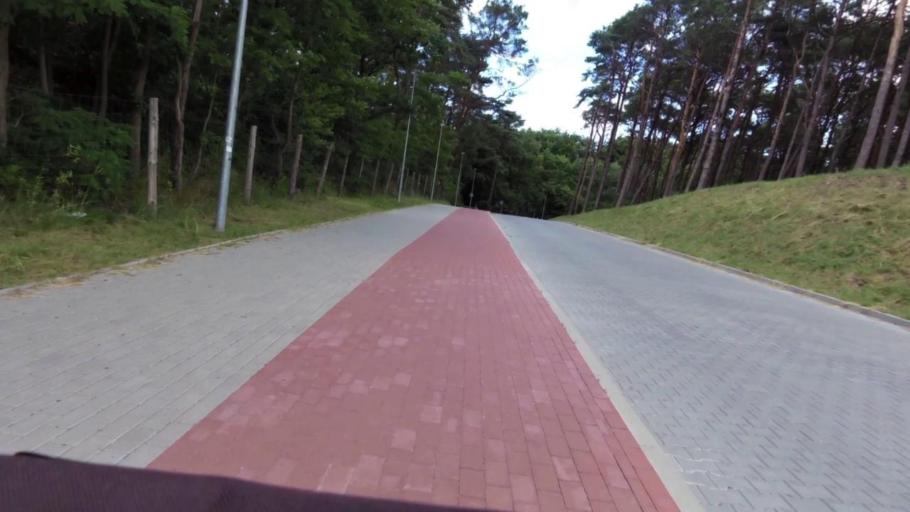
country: PL
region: West Pomeranian Voivodeship
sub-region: Powiat gryficki
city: Mrzezyno
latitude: 54.1432
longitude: 15.2846
